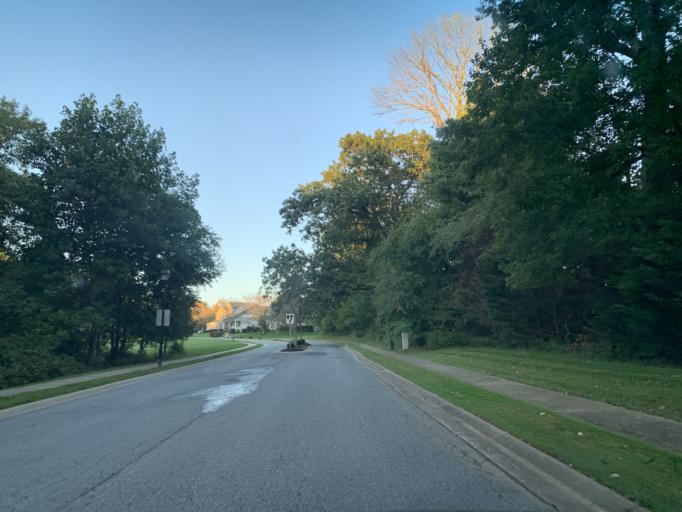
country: US
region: Maryland
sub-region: Harford County
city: Bel Air South
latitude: 39.5242
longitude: -76.2982
